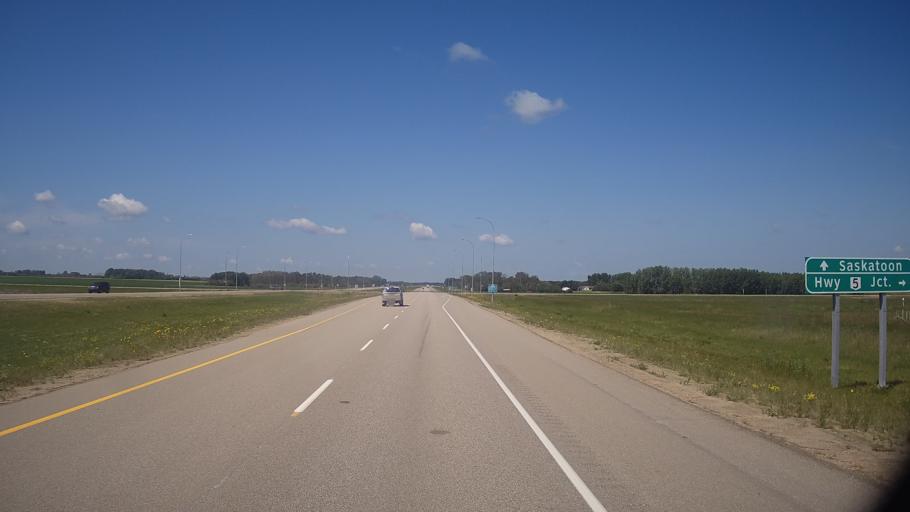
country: CA
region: Saskatchewan
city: Saskatoon
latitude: 52.0123
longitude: -106.3809
